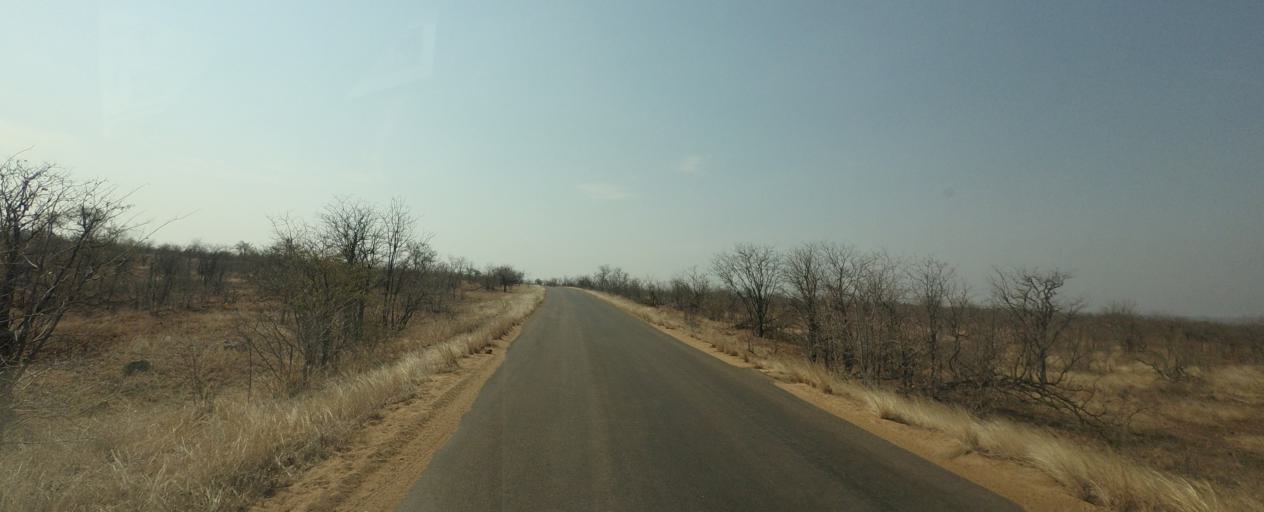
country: ZA
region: Limpopo
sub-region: Mopani District Municipality
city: Phalaborwa
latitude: -23.9447
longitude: 31.6144
